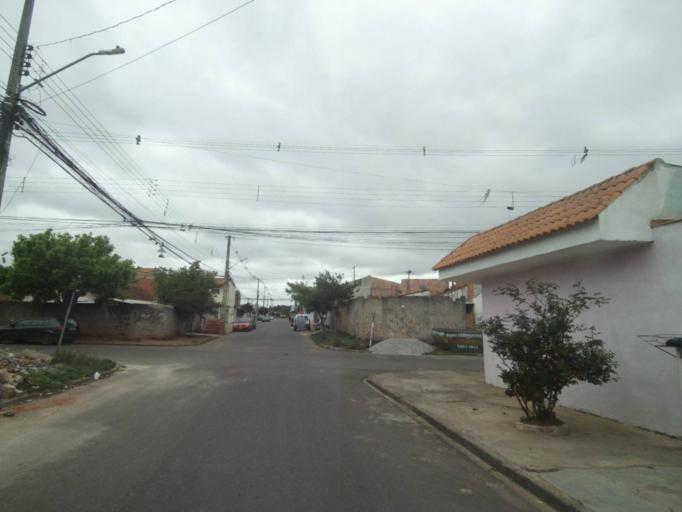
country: BR
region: Parana
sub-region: Sao Jose Dos Pinhais
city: Sao Jose dos Pinhais
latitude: -25.5565
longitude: -49.2658
